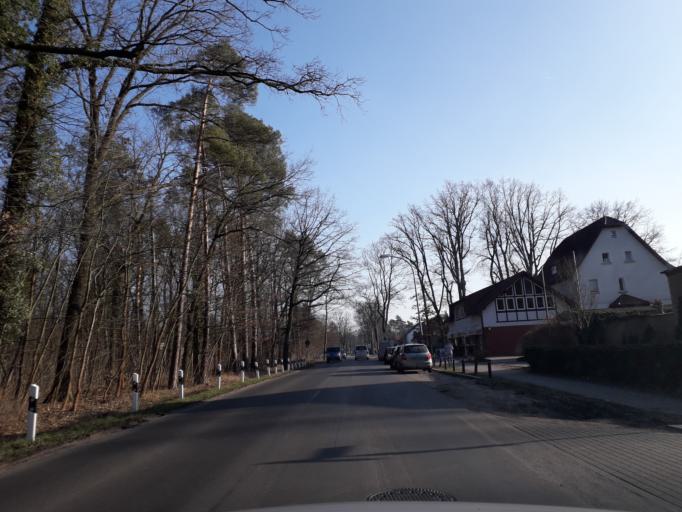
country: DE
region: Brandenburg
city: Falkensee
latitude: 52.5834
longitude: 13.0711
